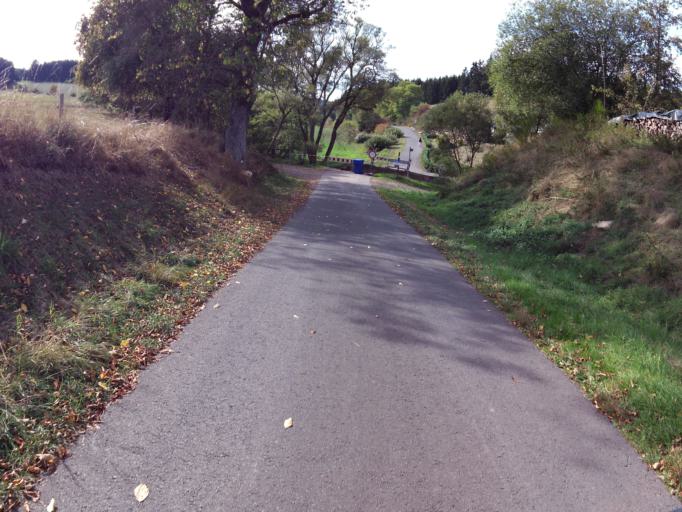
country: DE
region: Rheinland-Pfalz
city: Winterspelt
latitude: 50.2231
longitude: 6.2331
